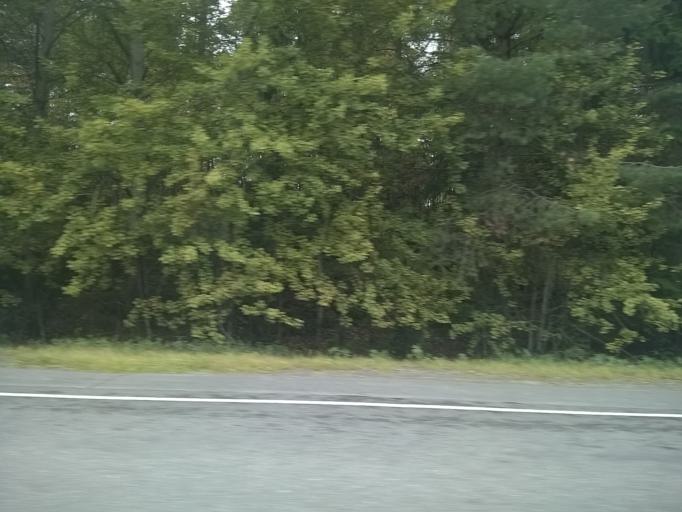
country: FI
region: Pirkanmaa
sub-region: Tampere
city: Tampere
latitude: 61.4645
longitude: 23.8419
